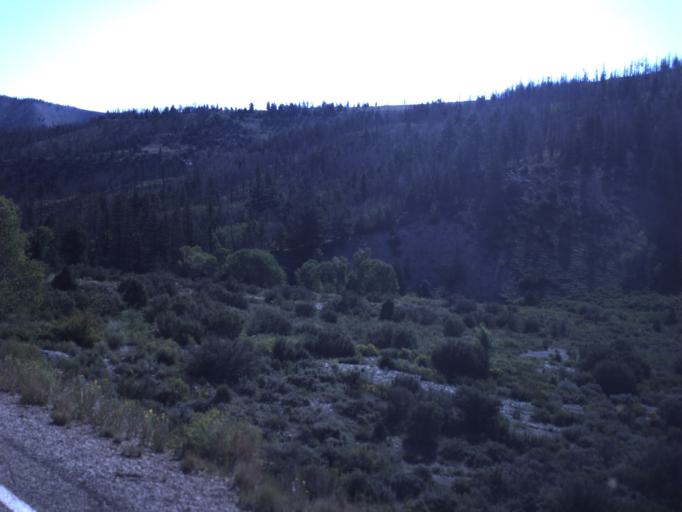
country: US
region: Utah
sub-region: Carbon County
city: Helper
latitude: 39.9123
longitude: -110.6987
